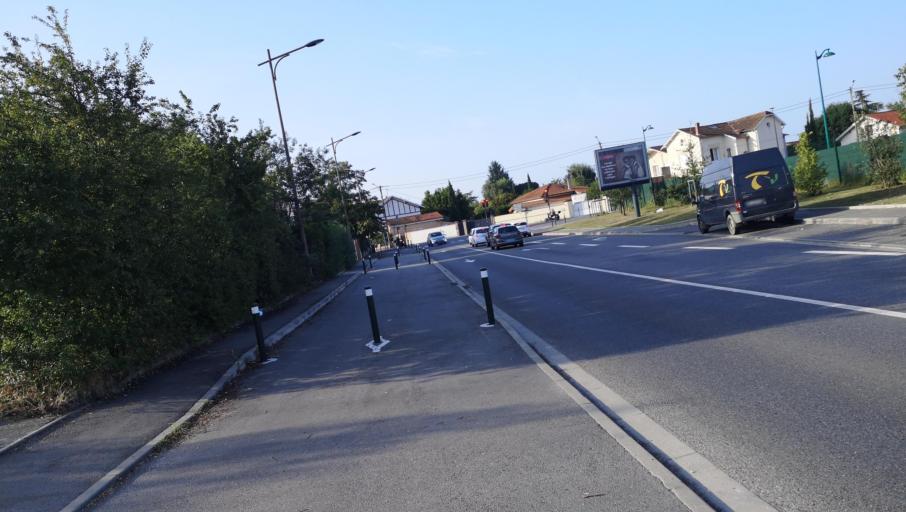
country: FR
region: Midi-Pyrenees
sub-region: Departement de la Haute-Garonne
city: Blagnac
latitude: 43.5942
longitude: 1.3934
